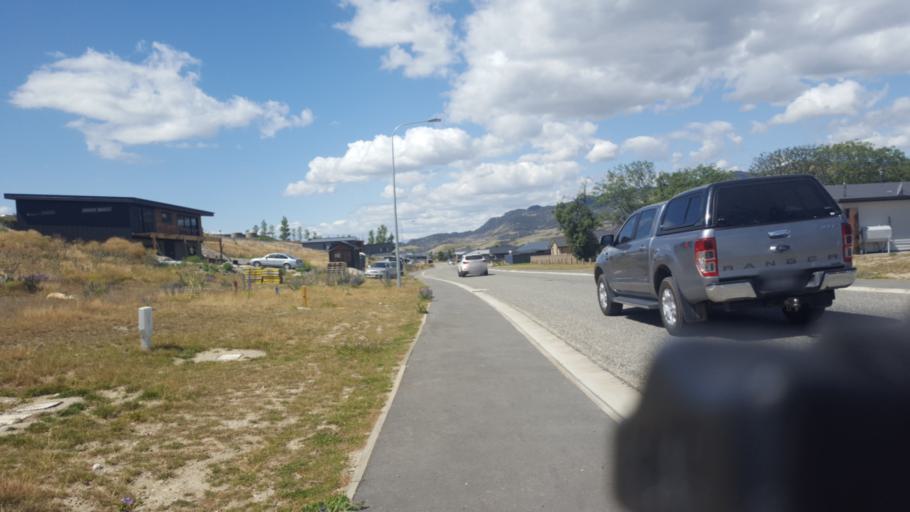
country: NZ
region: Otago
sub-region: Queenstown-Lakes District
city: Wanaka
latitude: -44.9750
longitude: 169.2398
